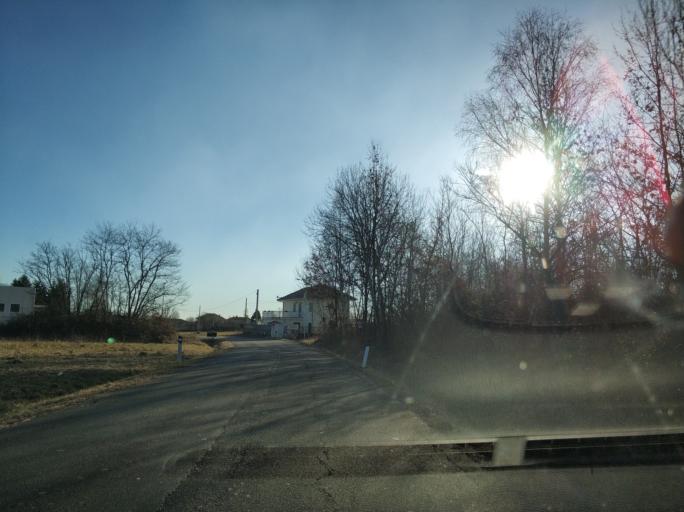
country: IT
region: Piedmont
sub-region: Provincia di Torino
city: Front
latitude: 45.2609
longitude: 7.6510
